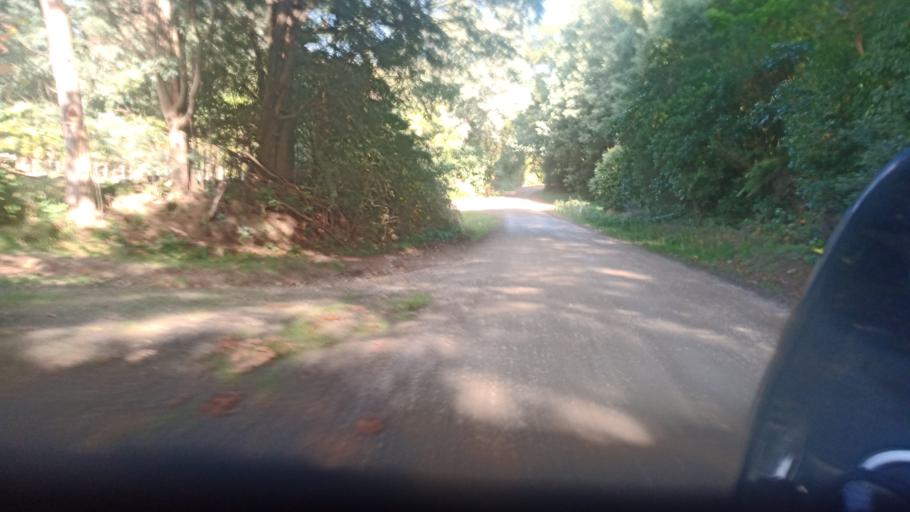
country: NZ
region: Bay of Plenty
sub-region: Opotiki District
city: Opotiki
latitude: -38.4398
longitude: 177.5374
